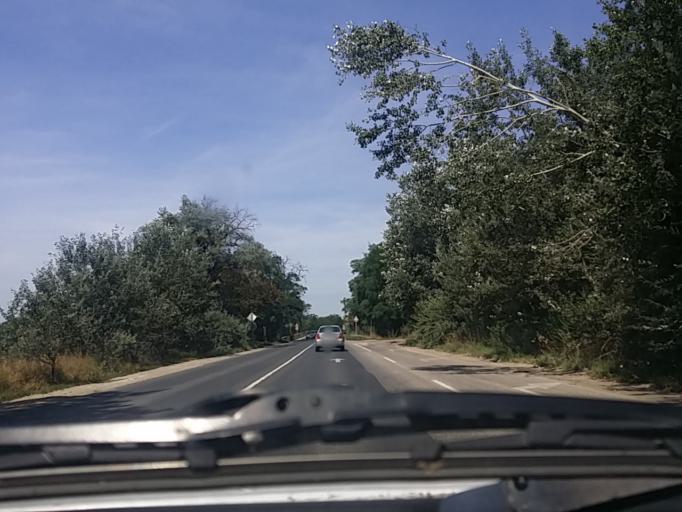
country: HU
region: Pest
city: Pilisborosjeno
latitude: 47.5933
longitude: 18.9823
